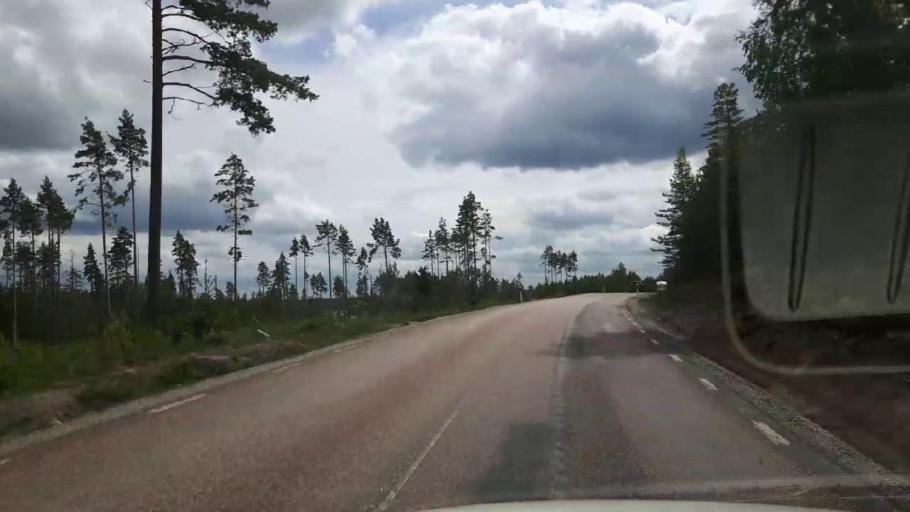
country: SE
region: Vaestmanland
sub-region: Skinnskattebergs Kommun
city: Skinnskatteberg
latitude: 59.8248
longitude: 15.8357
